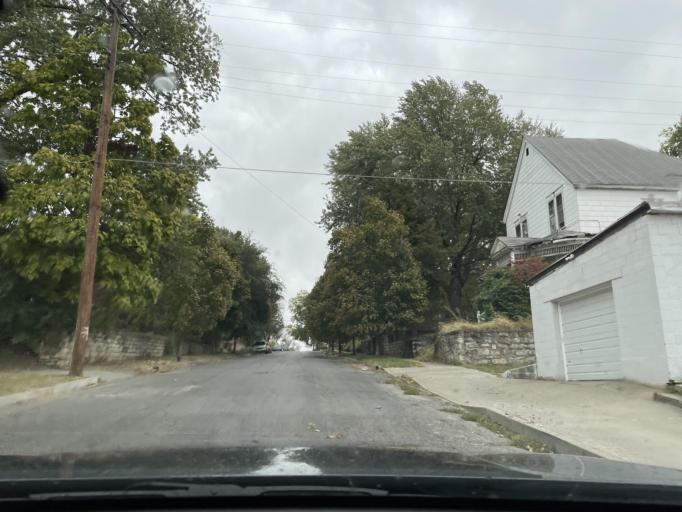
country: US
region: Missouri
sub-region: Buchanan County
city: Saint Joseph
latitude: 39.7717
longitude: -94.8478
